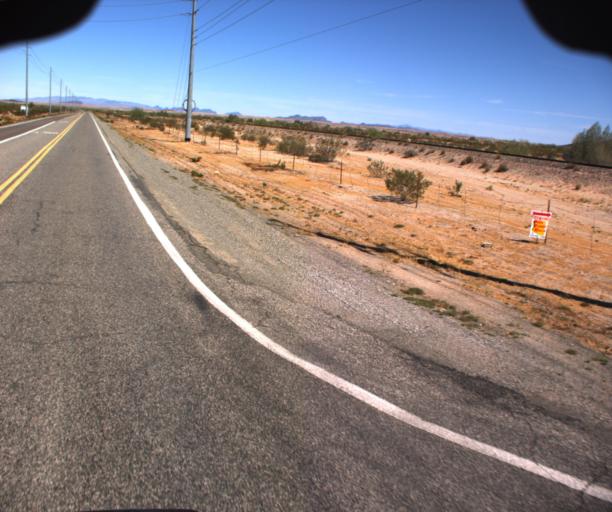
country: US
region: Arizona
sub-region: La Paz County
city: Cienega Springs
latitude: 33.9607
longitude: -114.0317
